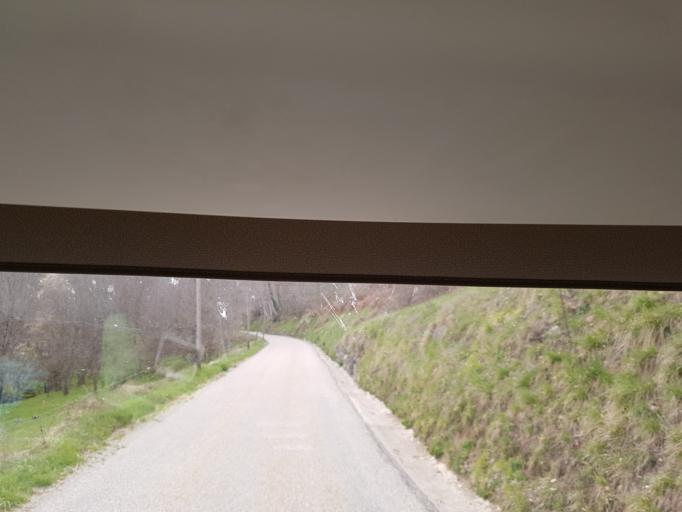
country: FR
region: Languedoc-Roussillon
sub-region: Departement de l'Aude
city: Quillan
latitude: 42.7328
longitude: 2.0795
